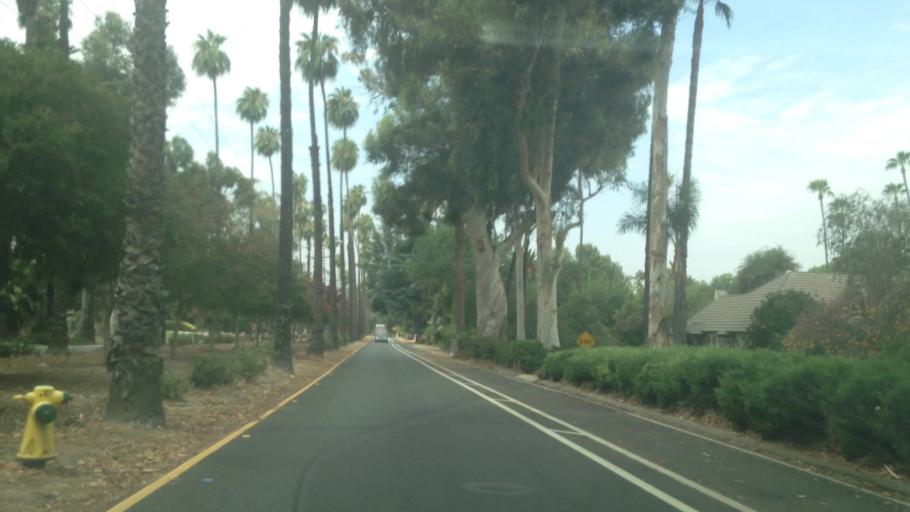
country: US
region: California
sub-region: Riverside County
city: Riverside
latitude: 33.9002
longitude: -117.4420
